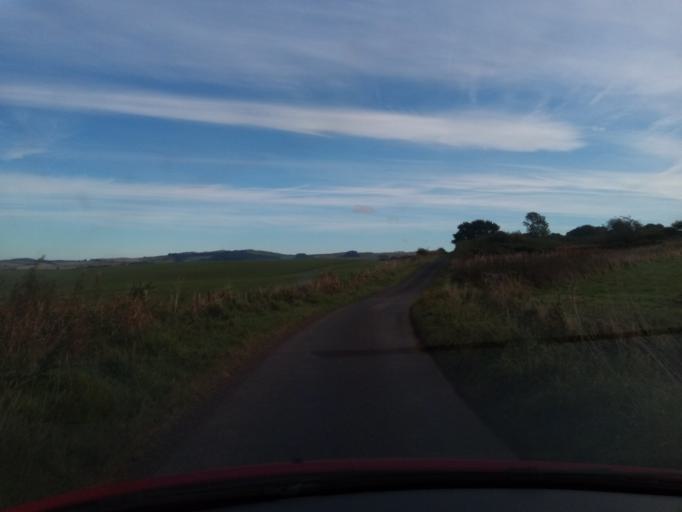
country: GB
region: Scotland
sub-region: The Scottish Borders
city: Kelso
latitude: 55.5129
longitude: -2.3988
